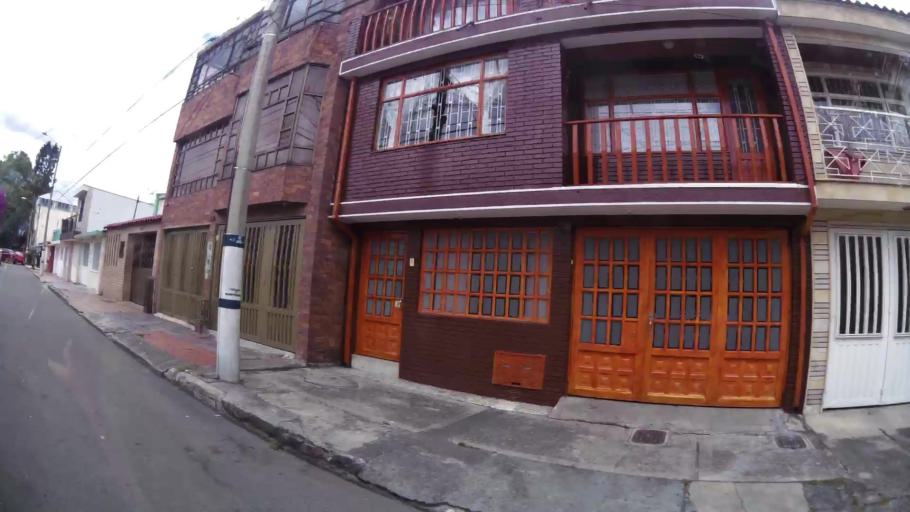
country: CO
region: Bogota D.C.
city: Bogota
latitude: 4.6007
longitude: -74.1138
